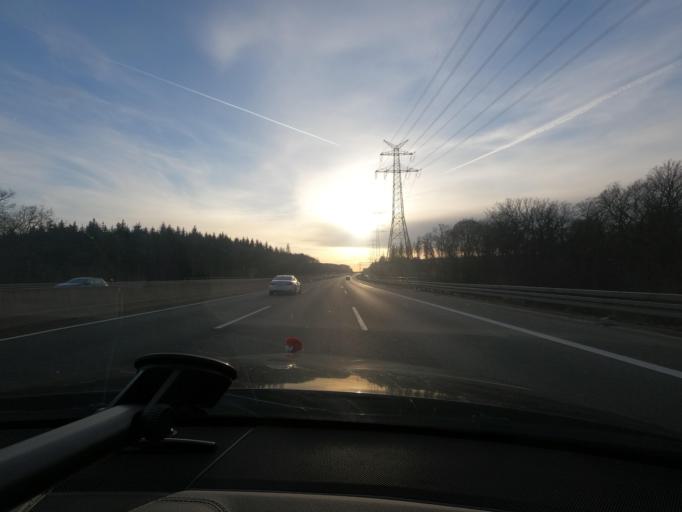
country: DE
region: Lower Saxony
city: Haverlah
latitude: 52.0515
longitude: 10.1877
